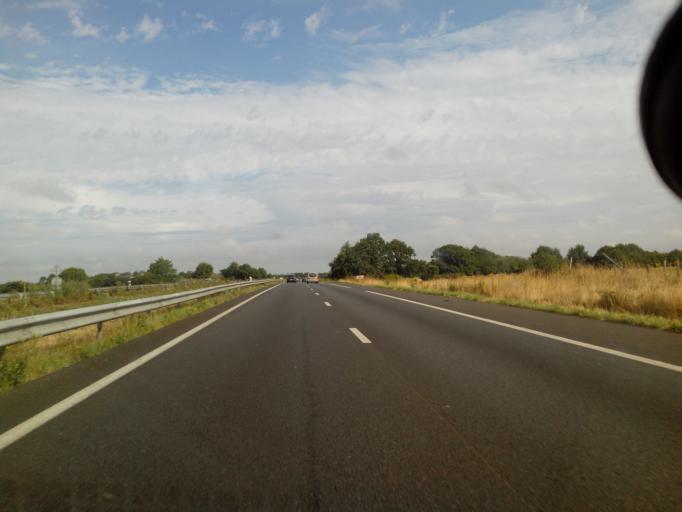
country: FR
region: Pays de la Loire
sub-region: Departement de la Loire-Atlantique
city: Vigneux-de-Bretagne
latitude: 47.3077
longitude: -1.7628
